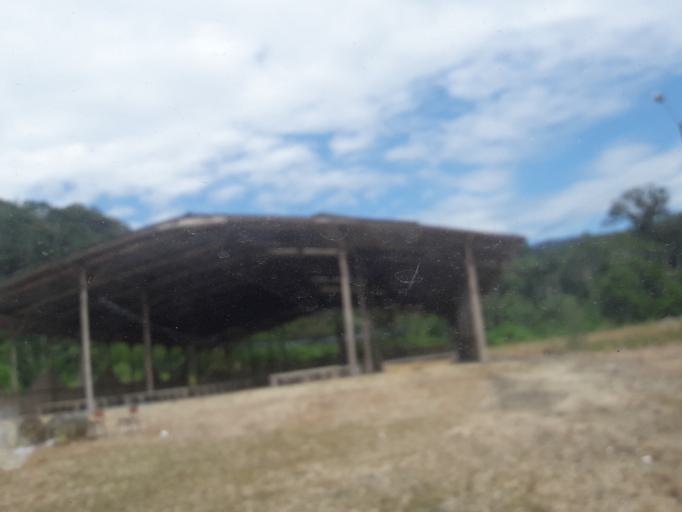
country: EC
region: Napo
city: Tena
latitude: -1.0673
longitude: -77.9086
